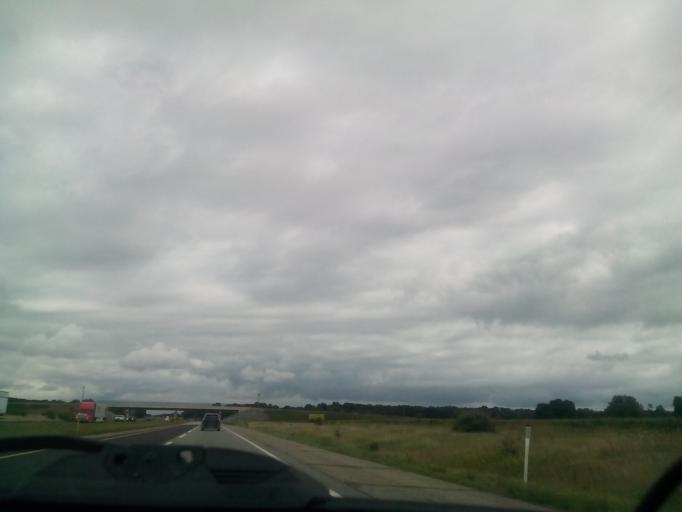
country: US
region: Michigan
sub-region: Saint Joseph County
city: Sturgis
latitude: 41.7435
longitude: -85.3198
